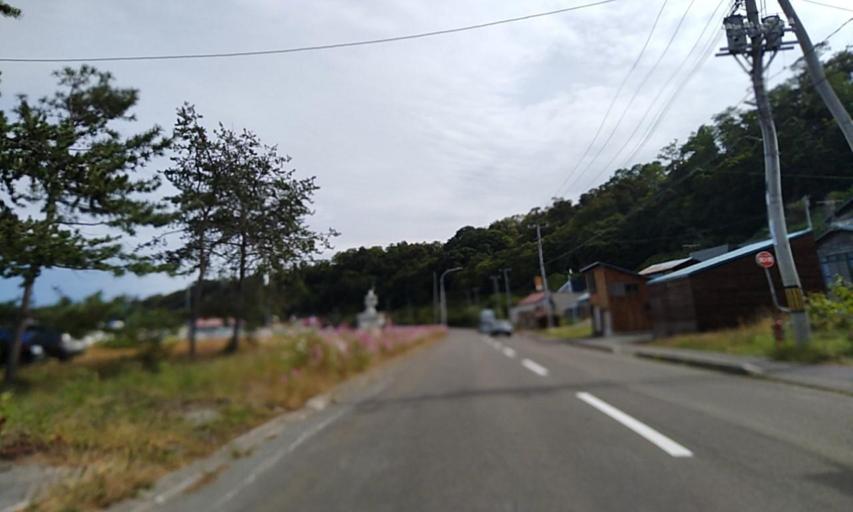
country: JP
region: Hokkaido
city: Rumoi
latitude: 43.8518
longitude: 141.5311
